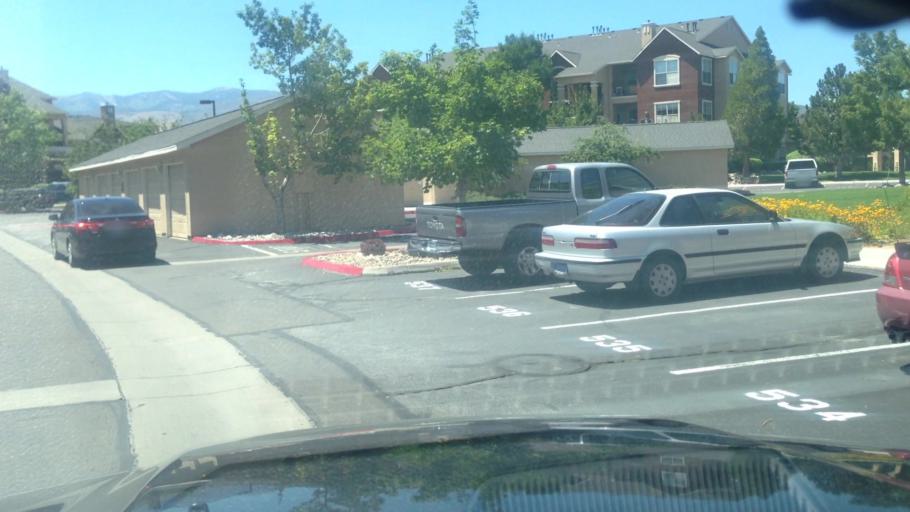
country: US
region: Nevada
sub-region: Washoe County
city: Sparks
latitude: 39.4407
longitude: -119.7540
